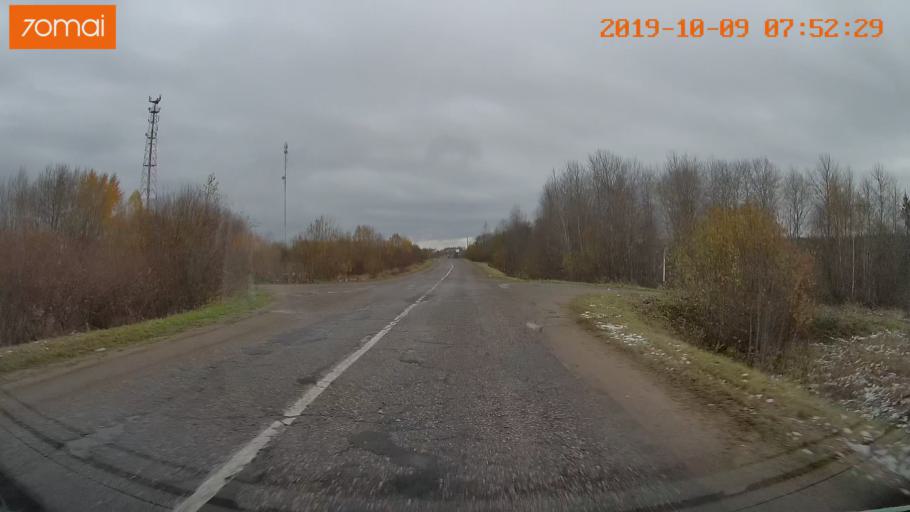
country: RU
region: Jaroslavl
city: Kukoboy
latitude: 58.6915
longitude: 39.8876
